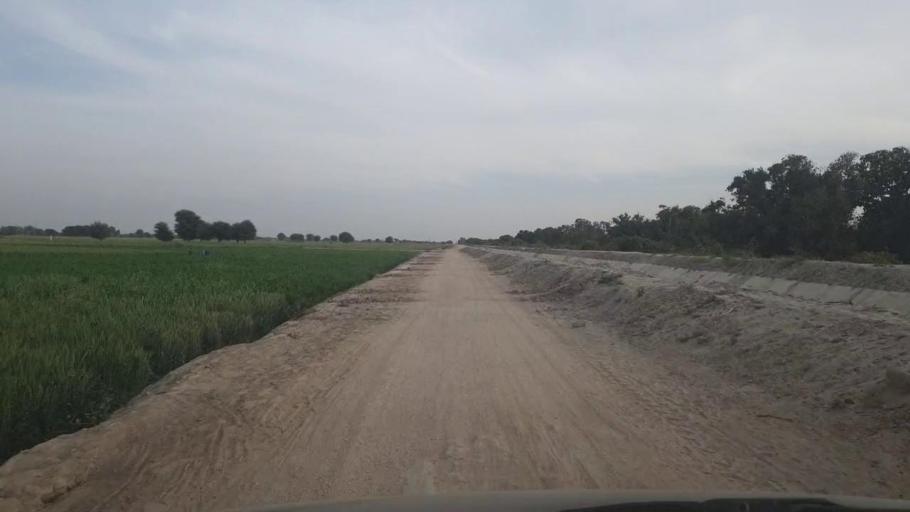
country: PK
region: Sindh
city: Kunri
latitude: 25.2717
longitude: 69.5617
